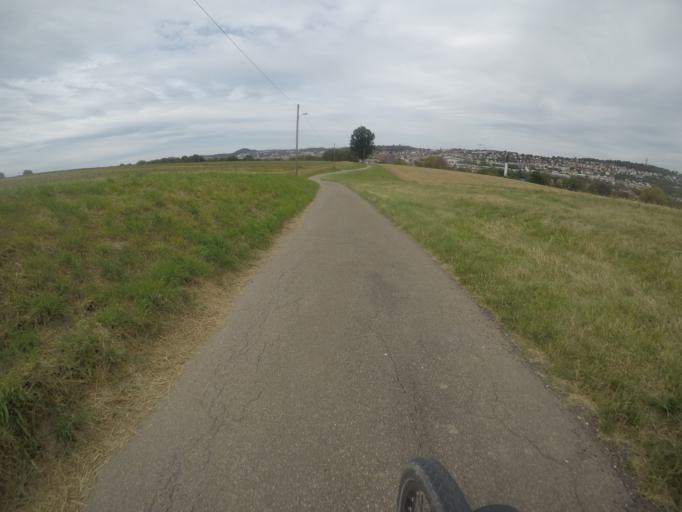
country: DE
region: Baden-Wuerttemberg
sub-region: Karlsruhe Region
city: Pforzheim
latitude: 48.8888
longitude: 8.7221
